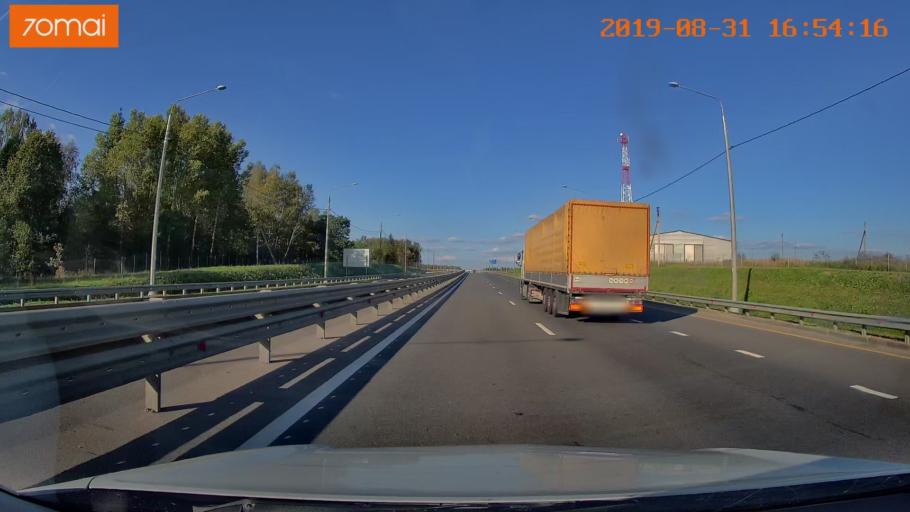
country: RU
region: Kaluga
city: Detchino
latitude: 54.7677
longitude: 36.2291
